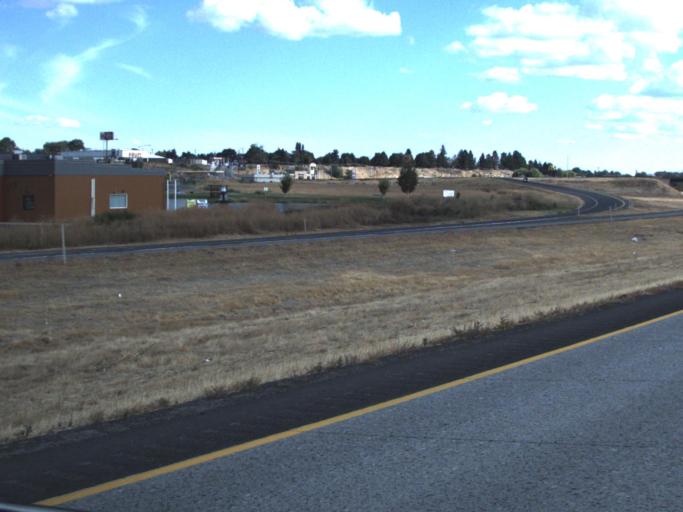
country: US
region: Washington
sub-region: Yakima County
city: Zillah
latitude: 46.4051
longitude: -120.2834
